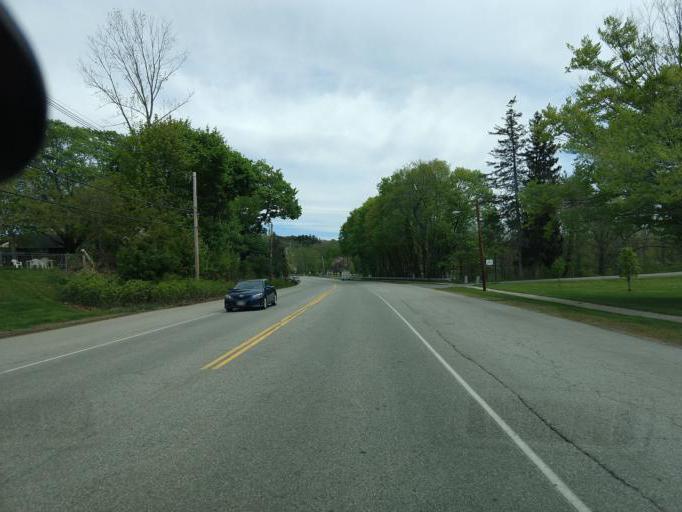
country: US
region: Massachusetts
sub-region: Essex County
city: Haverhill
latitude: 42.7890
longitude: -71.0702
